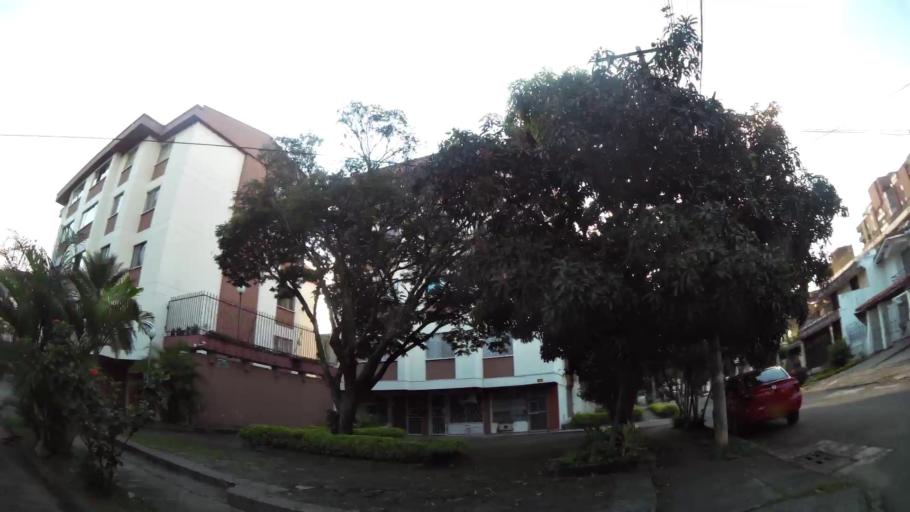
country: CO
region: Valle del Cauca
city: Cali
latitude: 3.4070
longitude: -76.5546
